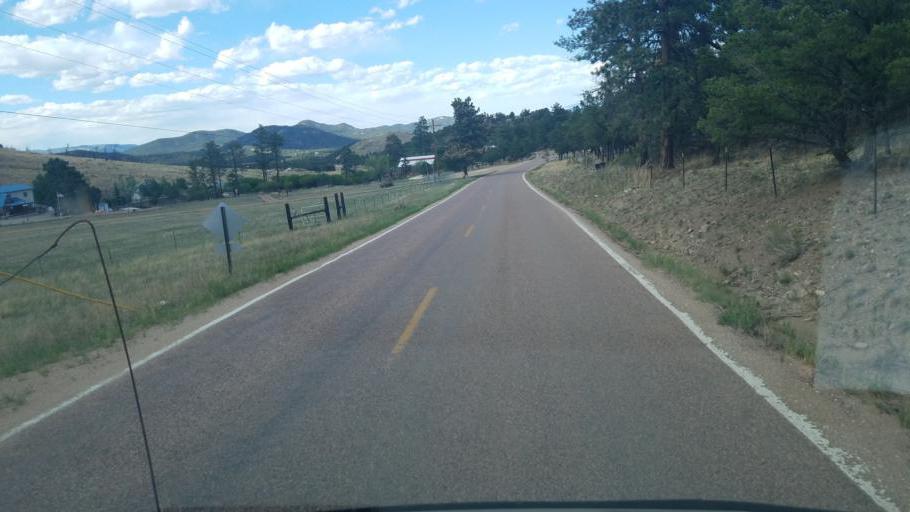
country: US
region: Colorado
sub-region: Custer County
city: Westcliffe
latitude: 38.3257
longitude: -105.4871
